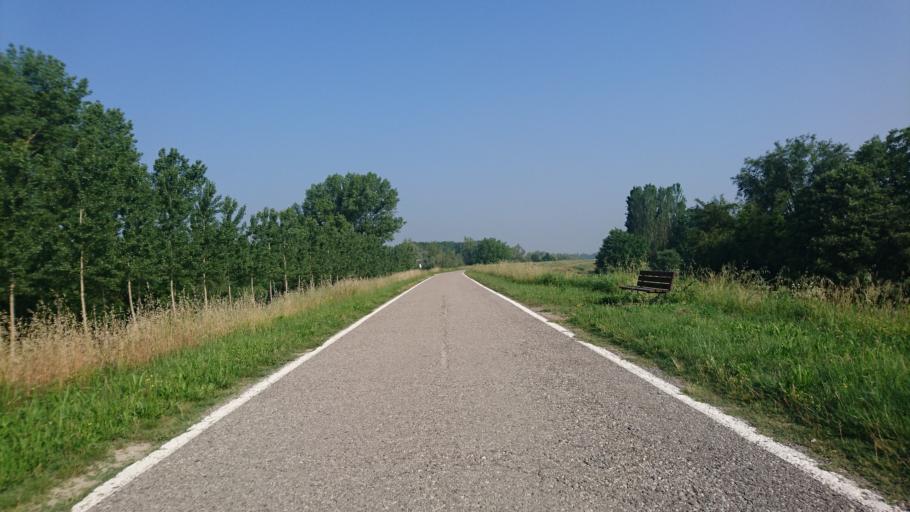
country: IT
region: Veneto
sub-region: Provincia di Rovigo
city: Castelnovo Bariano
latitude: 45.0230
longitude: 11.2745
